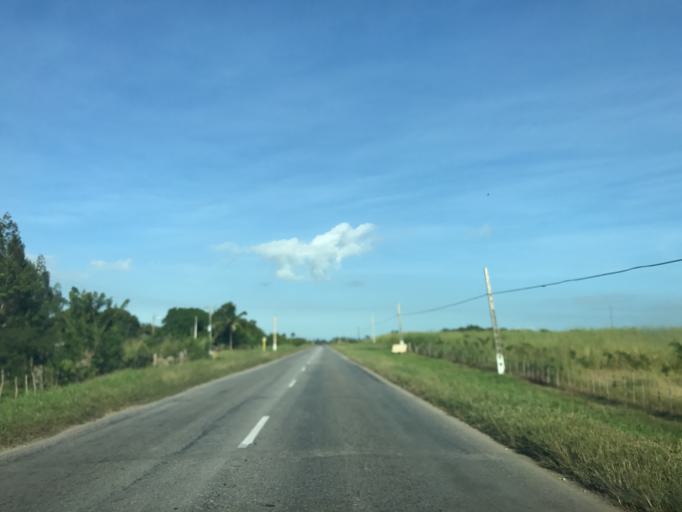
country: CU
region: Camaguey
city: Florida
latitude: 21.4814
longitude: -78.1805
